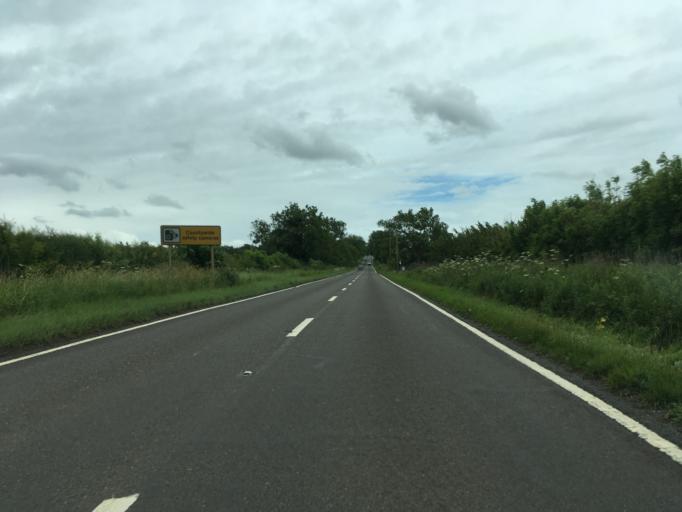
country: GB
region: England
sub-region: Northamptonshire
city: Daventry
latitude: 52.2493
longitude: -1.2338
